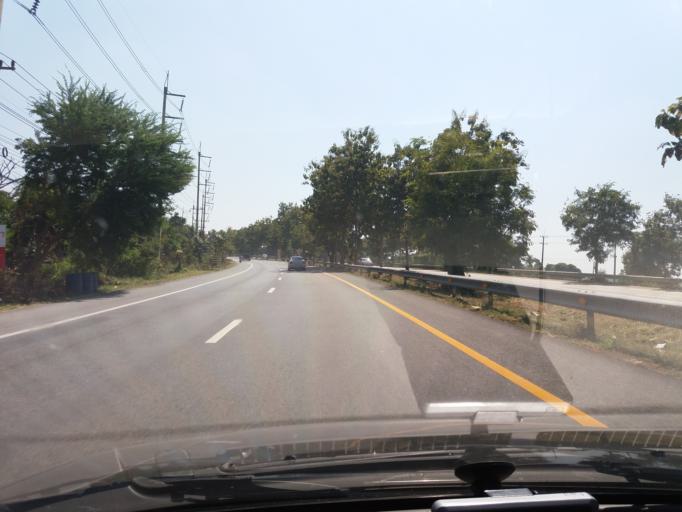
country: TH
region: Chai Nat
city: Sankhaburi
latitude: 15.1044
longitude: 100.1364
